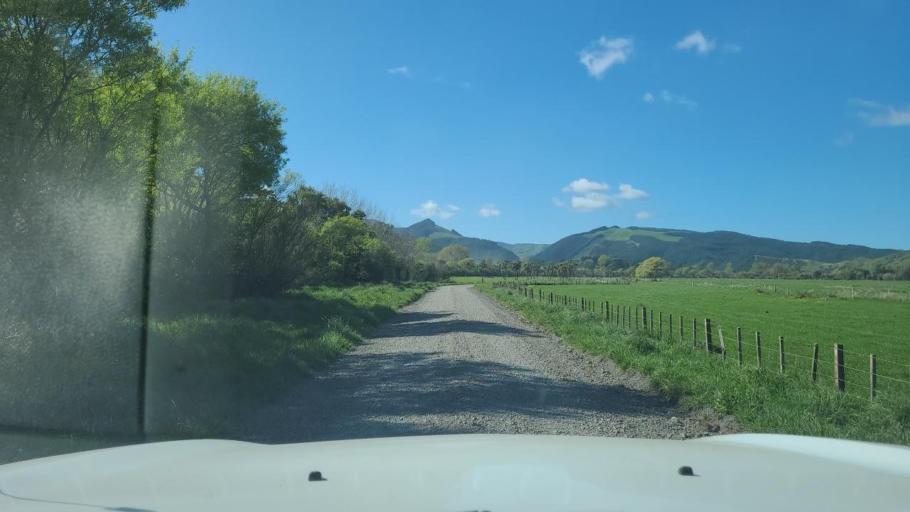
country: NZ
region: Wellington
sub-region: Upper Hutt City
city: Upper Hutt
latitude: -41.3813
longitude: 175.2157
